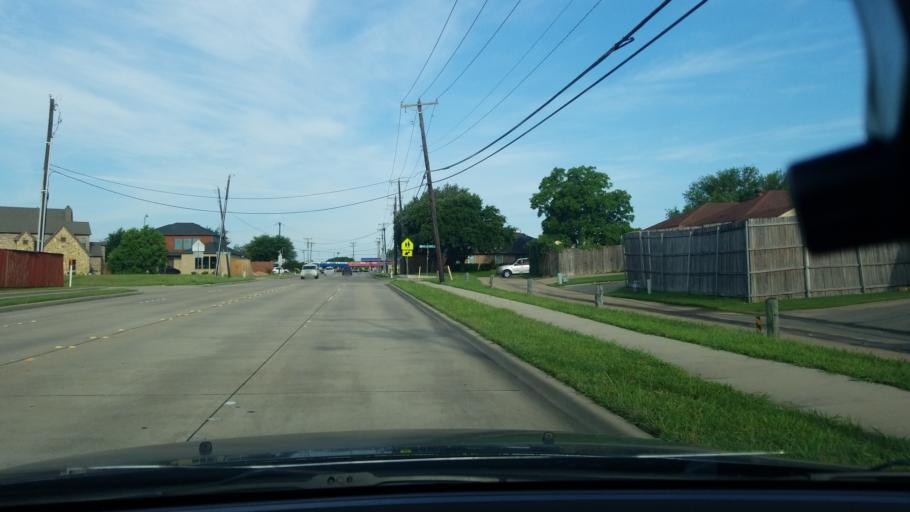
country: US
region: Texas
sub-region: Dallas County
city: Mesquite
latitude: 32.7978
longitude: -96.6081
